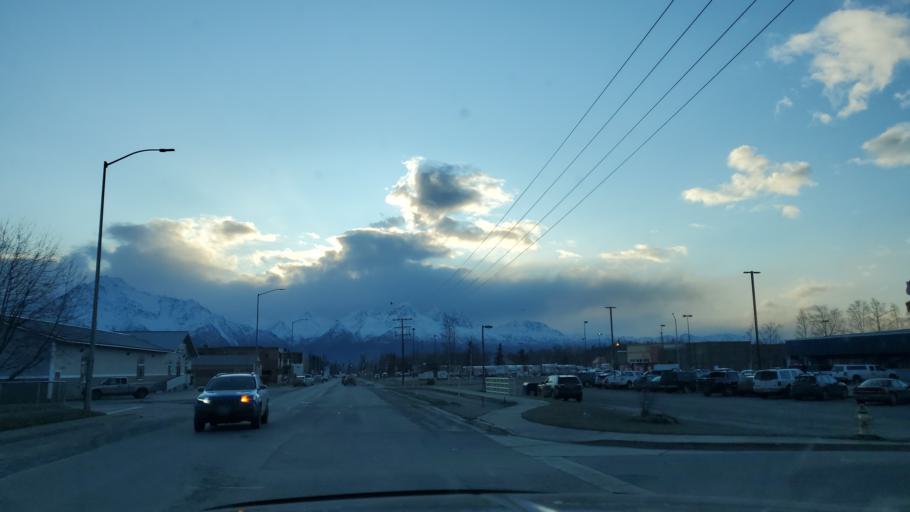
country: US
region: Alaska
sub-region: Matanuska-Susitna Borough
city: Palmer
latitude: 61.6028
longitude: -149.1183
